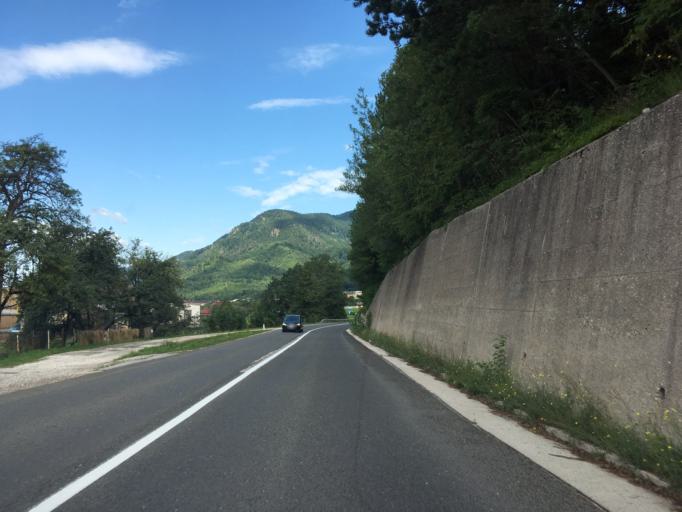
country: SI
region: Jesenice
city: Slovenski Javornik
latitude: 46.4193
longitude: 14.1076
